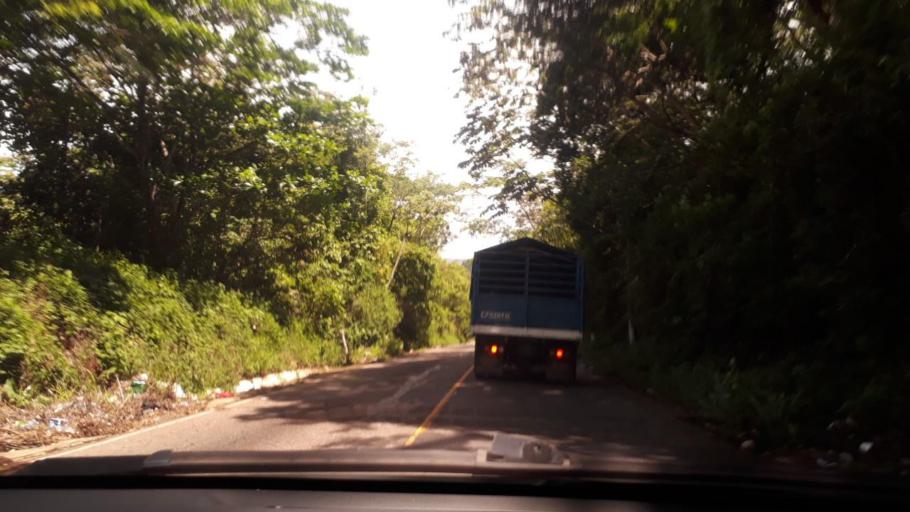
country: GT
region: Jutiapa
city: Jalpatagua
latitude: 14.1778
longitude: -90.0480
